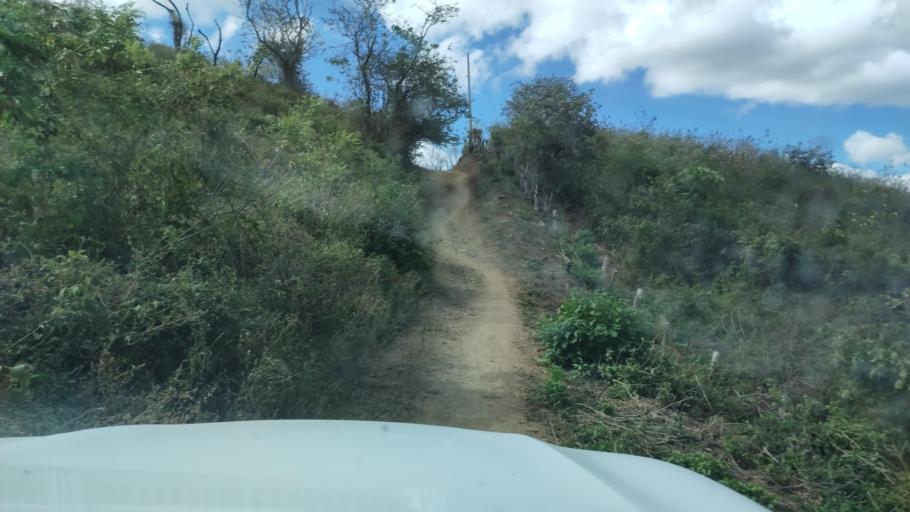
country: NI
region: Carazo
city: Santa Teresa
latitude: 11.6481
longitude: -86.2128
